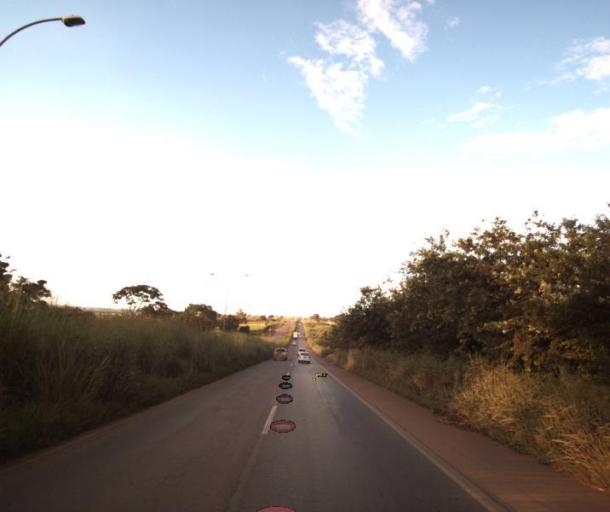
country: BR
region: Goias
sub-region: Anapolis
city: Anapolis
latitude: -16.3495
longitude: -48.9272
